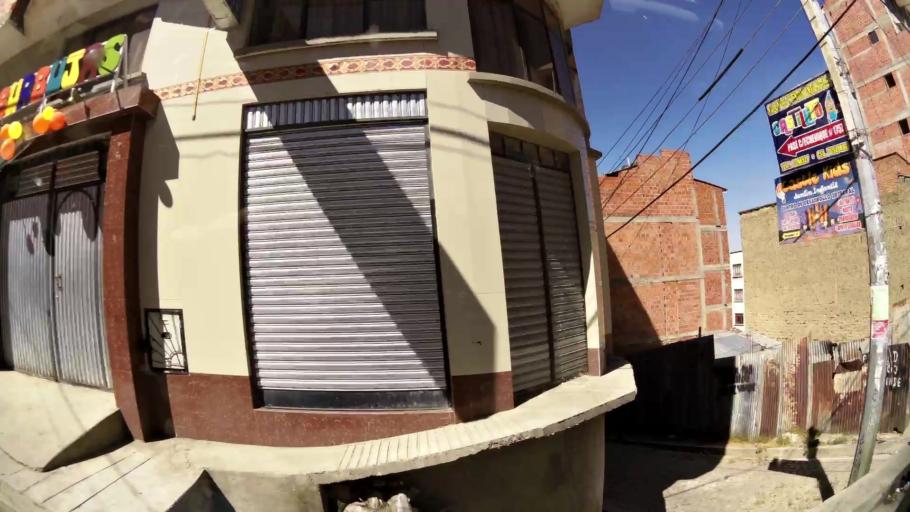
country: BO
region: La Paz
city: La Paz
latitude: -16.4905
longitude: -68.1550
